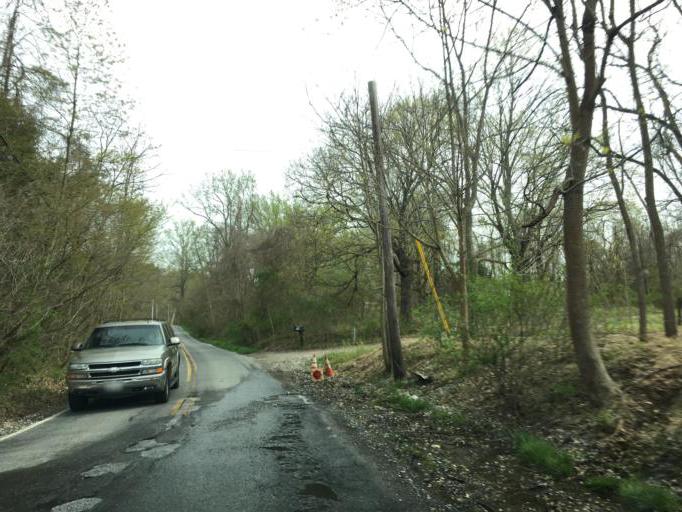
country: US
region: Maryland
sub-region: Baltimore County
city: Hunt Valley
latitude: 39.5312
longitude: -76.6150
